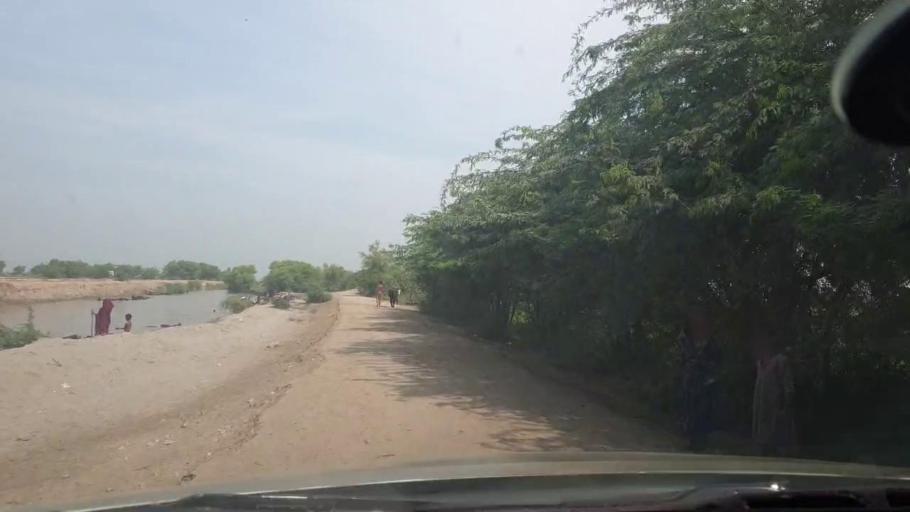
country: PK
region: Sindh
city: Jacobabad
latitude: 28.2987
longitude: 68.4762
